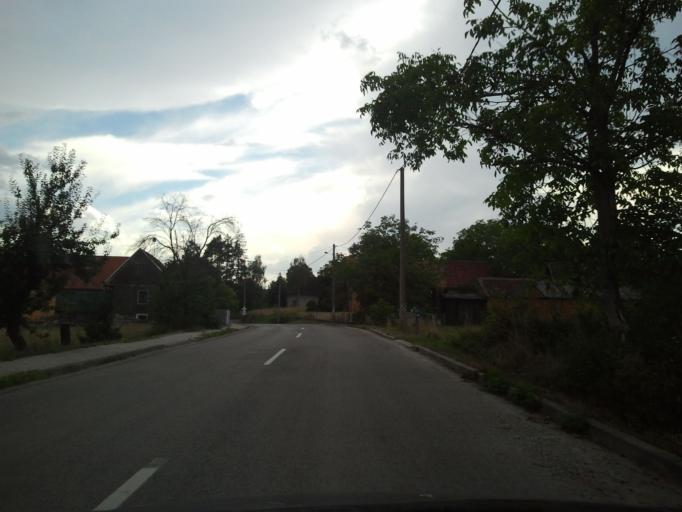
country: HR
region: Sisacko-Moslavacka
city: Glina
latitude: 45.4817
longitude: 15.9973
